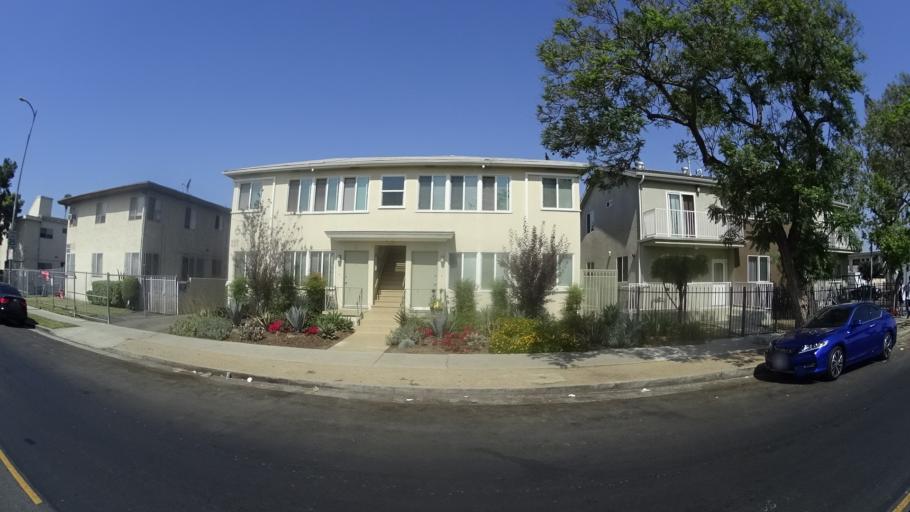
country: US
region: California
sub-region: Los Angeles County
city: View Park-Windsor Hills
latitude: 33.9828
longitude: -118.3265
